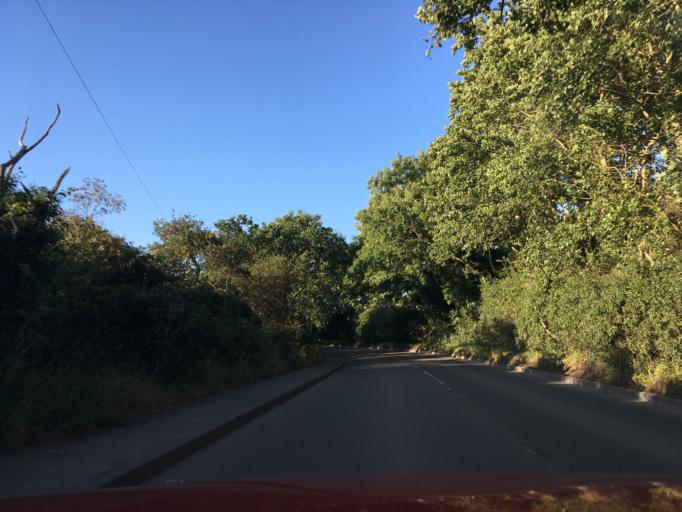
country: GB
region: England
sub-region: Hampshire
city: Tadley
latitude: 51.3675
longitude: -1.1534
